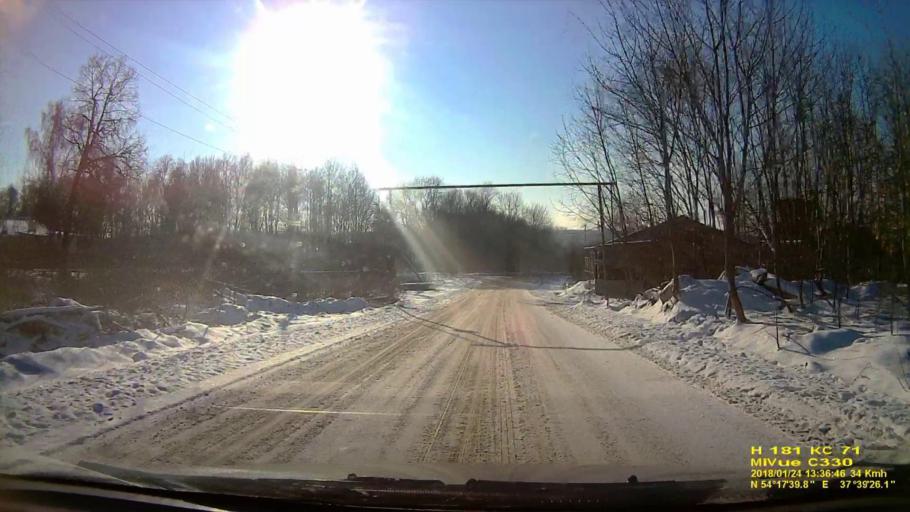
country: RU
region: Tula
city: Gorelki
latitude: 54.2943
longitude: 37.6572
